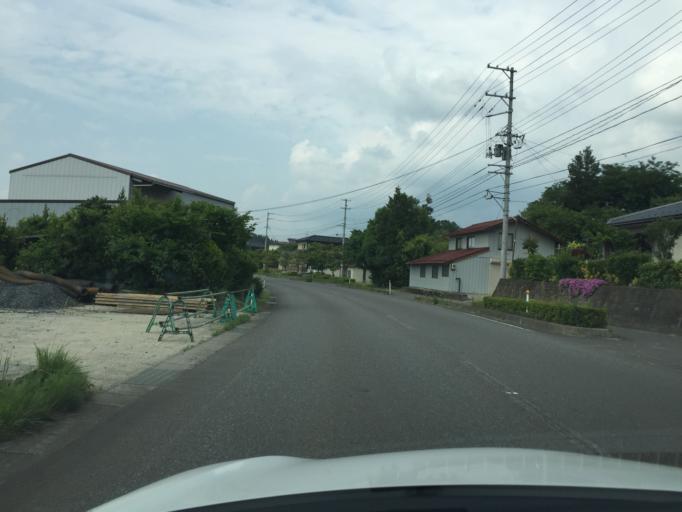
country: JP
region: Fukushima
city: Sukagawa
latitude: 37.2682
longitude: 140.4185
